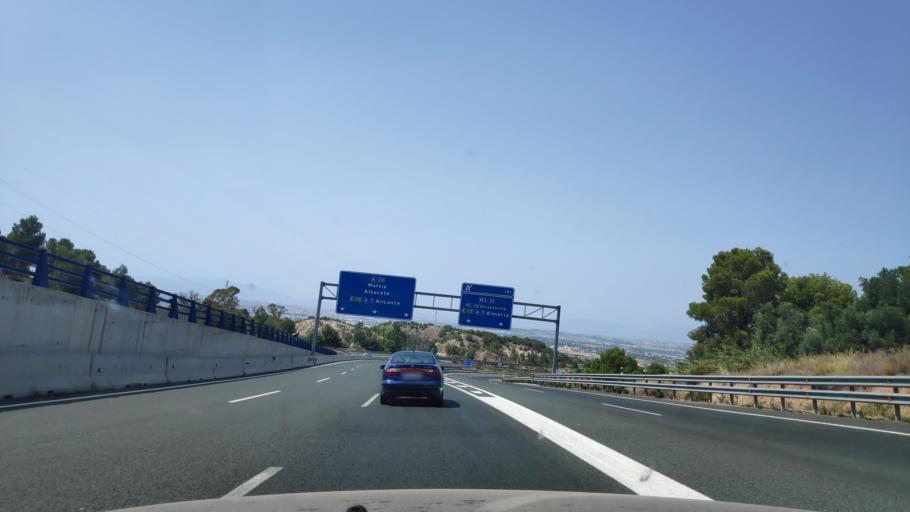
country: ES
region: Murcia
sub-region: Murcia
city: Alcantarilla
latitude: 37.9117
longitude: -1.1638
